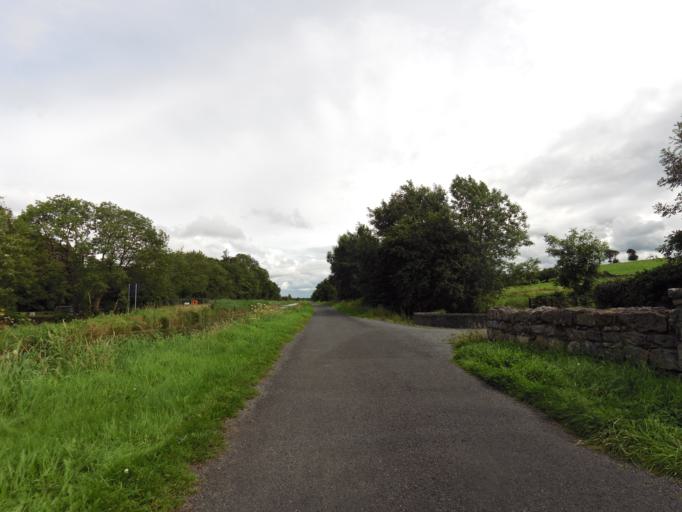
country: IE
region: Leinster
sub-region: An Longfort
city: Edgeworthstown
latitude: 53.5814
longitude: -7.5379
